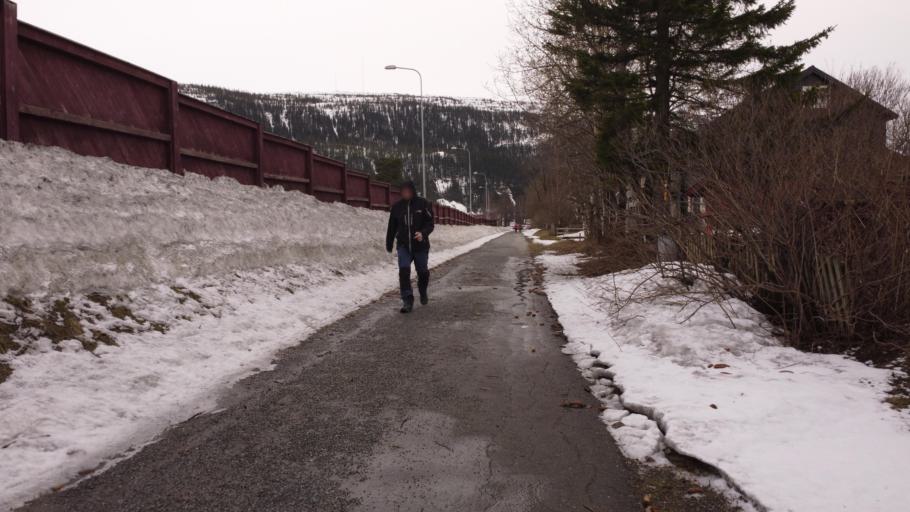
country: NO
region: Nordland
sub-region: Rana
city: Mo i Rana
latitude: 66.3127
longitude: 14.1551
